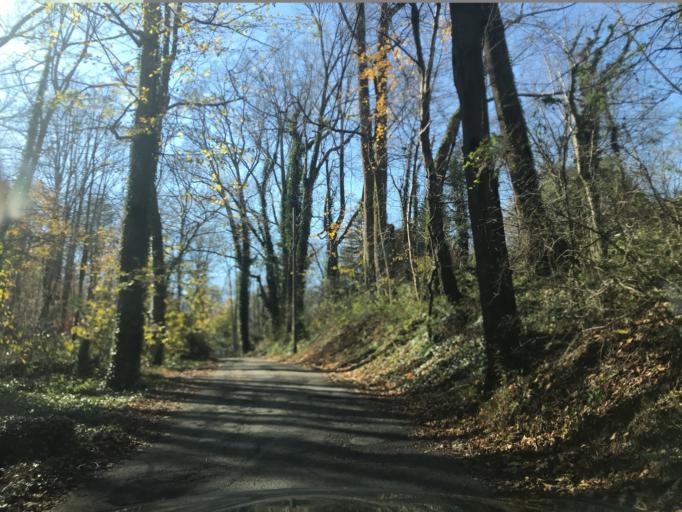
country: US
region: Maryland
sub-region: Baltimore County
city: Perry Hall
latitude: 39.4519
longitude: -76.4806
